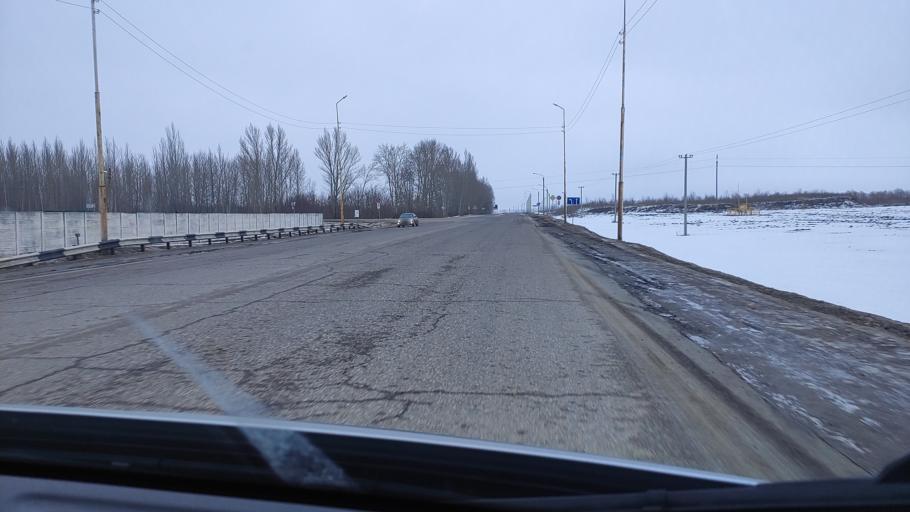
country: RU
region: Tambov
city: Mordovo
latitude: 52.0910
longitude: 40.8061
